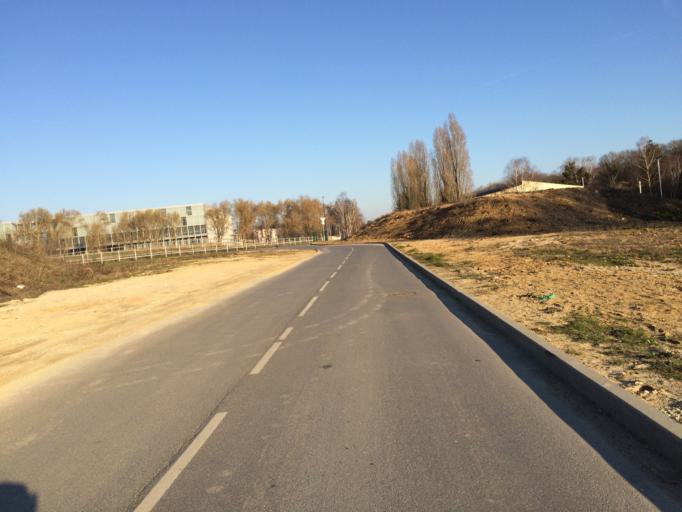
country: FR
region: Ile-de-France
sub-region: Departement de l'Essonne
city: Orsay
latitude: 48.7105
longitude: 2.2042
